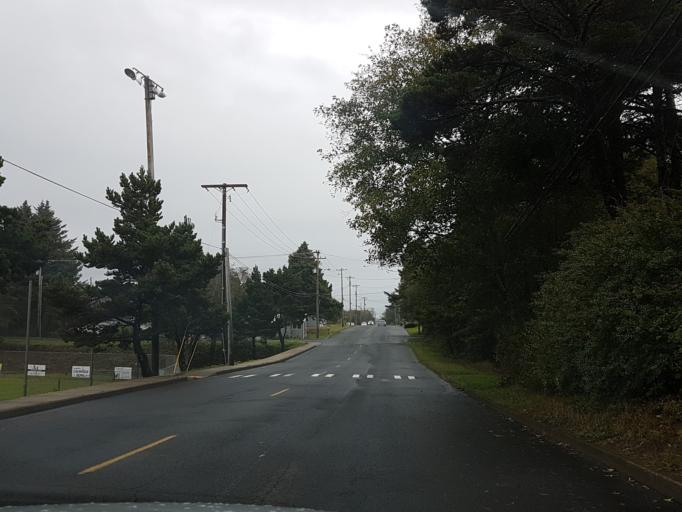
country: US
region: Oregon
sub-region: Lincoln County
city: Newport
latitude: 44.6429
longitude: -124.0557
